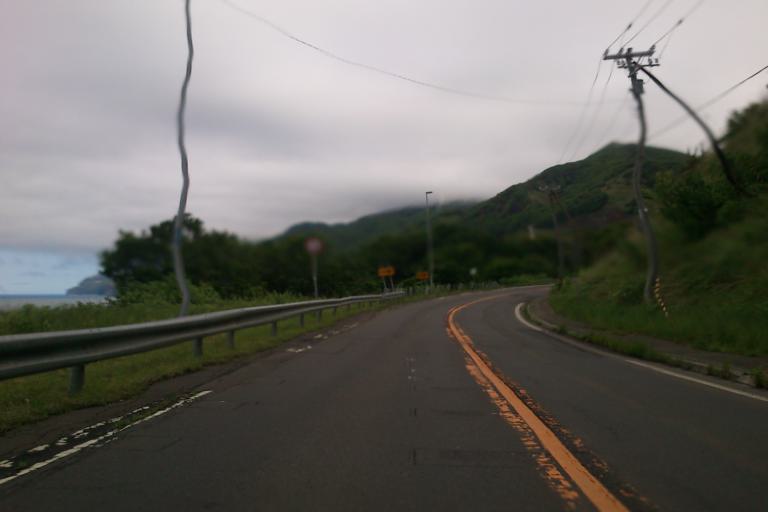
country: JP
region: Hokkaido
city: Ishikari
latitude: 43.4101
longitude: 141.4302
